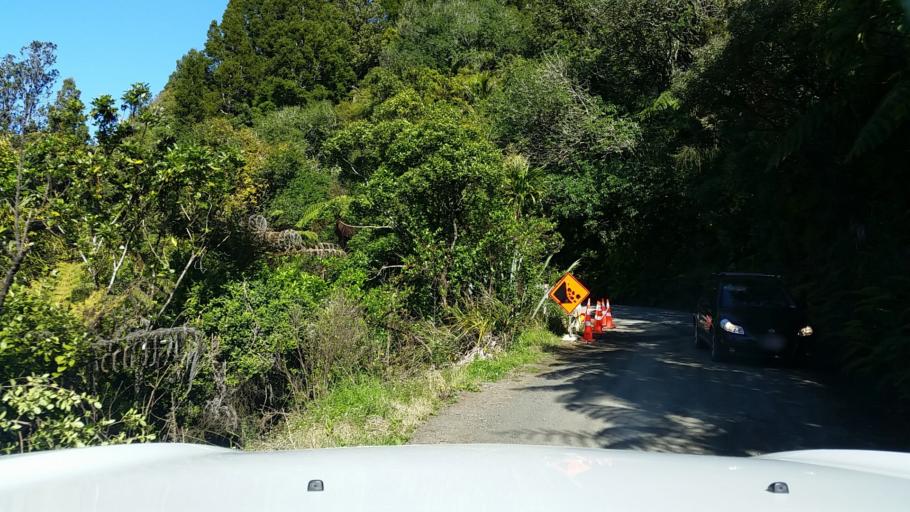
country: NZ
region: Auckland
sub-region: Auckland
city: Titirangi
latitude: -37.0257
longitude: 174.5310
